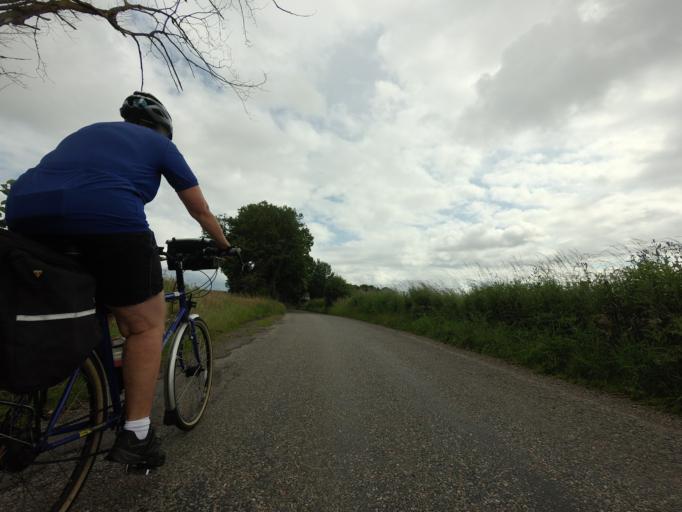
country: GB
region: Scotland
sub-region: Moray
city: Lhanbryd
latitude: 57.6467
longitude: -3.2487
